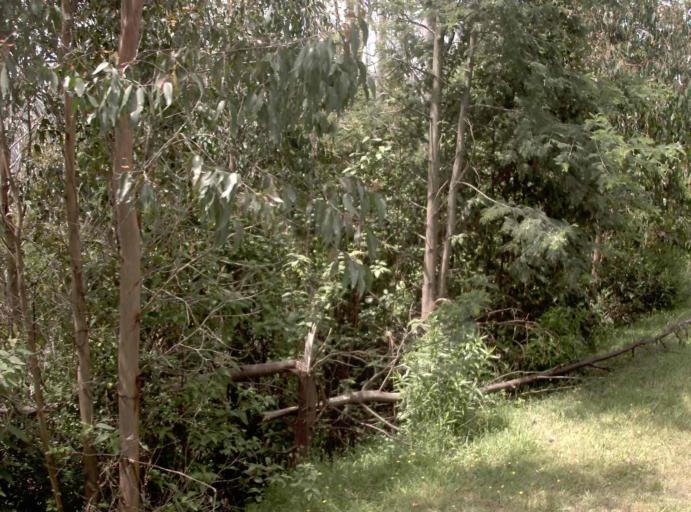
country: AU
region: Victoria
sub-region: Latrobe
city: Traralgon
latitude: -38.4310
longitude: 146.5517
